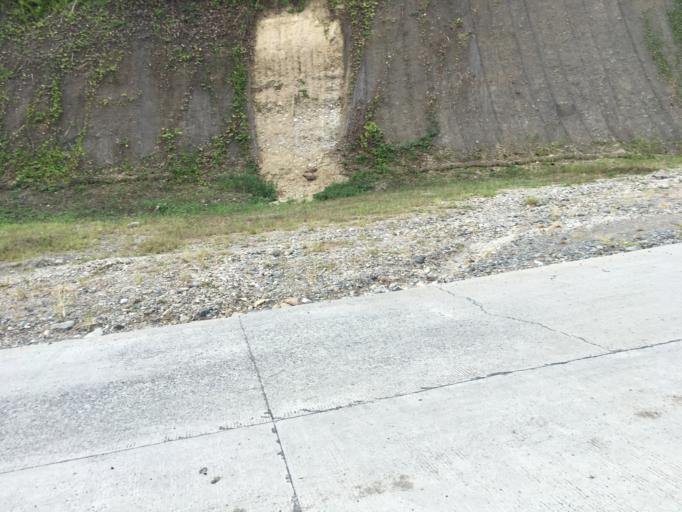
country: PH
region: Davao
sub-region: Province of Davao del Norte
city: New Bohol
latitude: 7.5037
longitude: 125.8790
